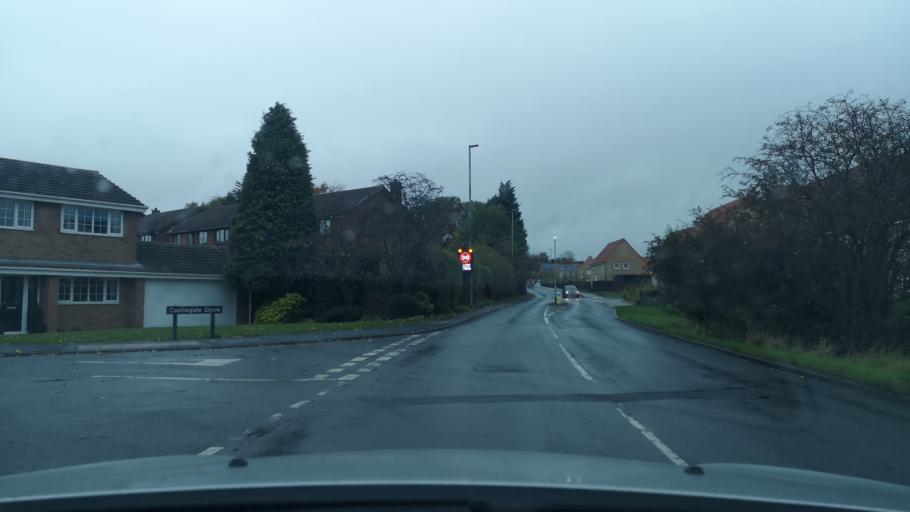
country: GB
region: England
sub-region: City and Borough of Wakefield
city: Pontefract
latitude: 53.6752
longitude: -1.3180
